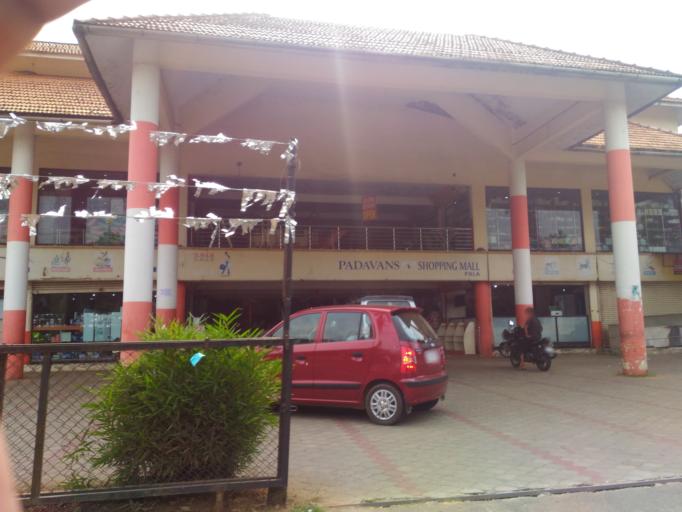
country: IN
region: Kerala
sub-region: Kottayam
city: Lalam
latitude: 9.7176
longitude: 76.6824
